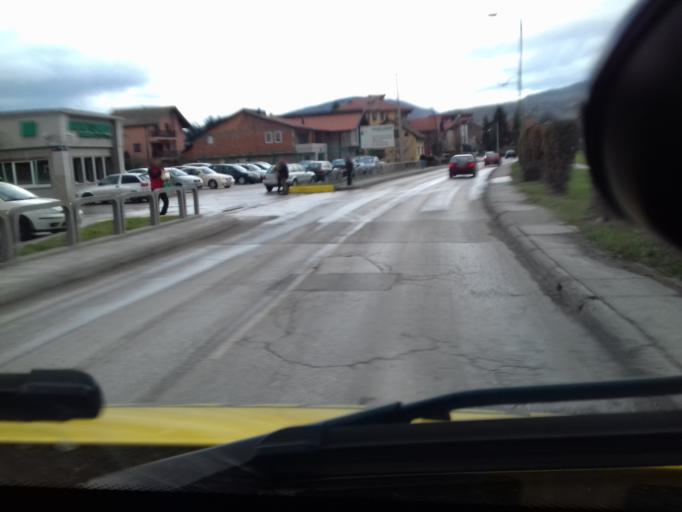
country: BA
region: Federation of Bosnia and Herzegovina
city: Kakanj
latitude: 44.1189
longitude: 18.1148
